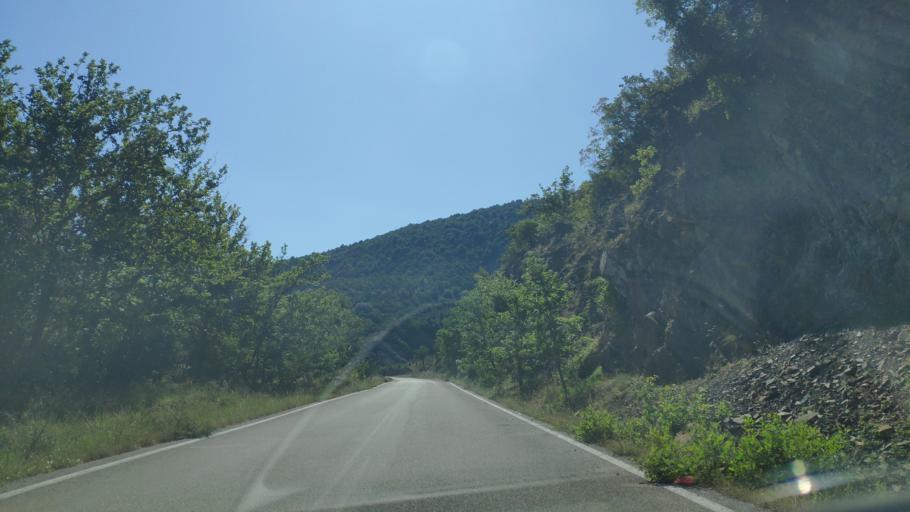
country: GR
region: West Greece
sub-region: Nomos Aitolias kai Akarnanias
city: Sardinia
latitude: 38.9223
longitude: 21.3636
